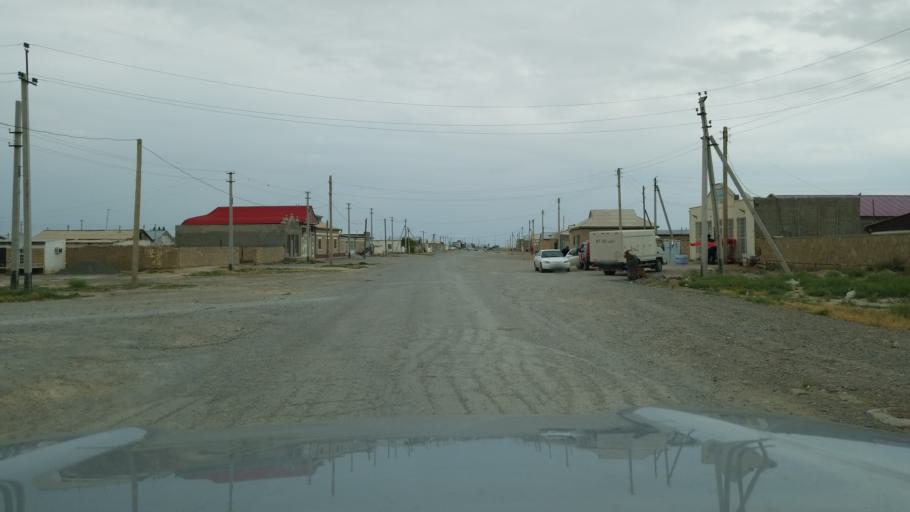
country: TM
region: Balkan
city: Serdar
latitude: 38.9913
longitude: 56.2775
